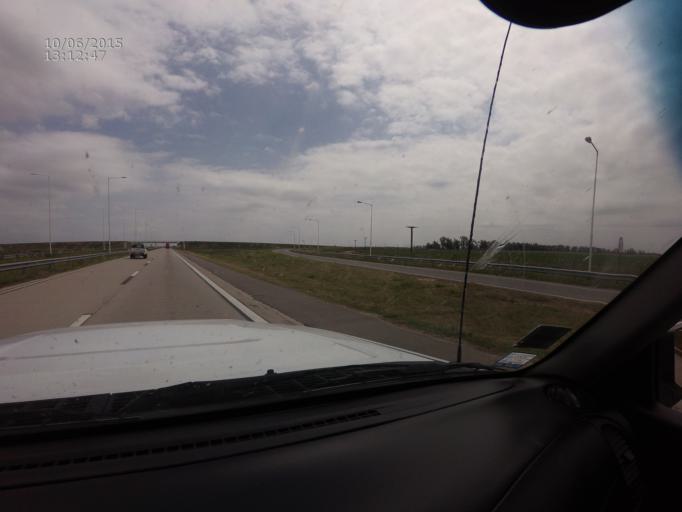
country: AR
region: Cordoba
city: General Roca
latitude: -32.7102
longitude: -61.9070
